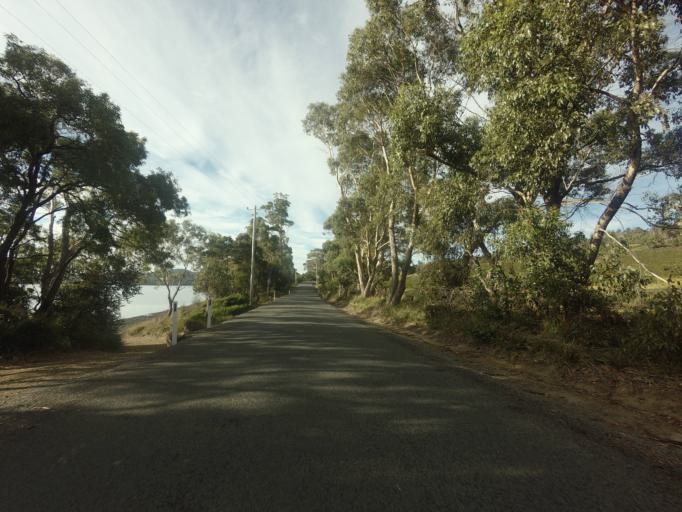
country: AU
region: Tasmania
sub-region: Sorell
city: Sorell
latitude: -42.9651
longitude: 147.8315
